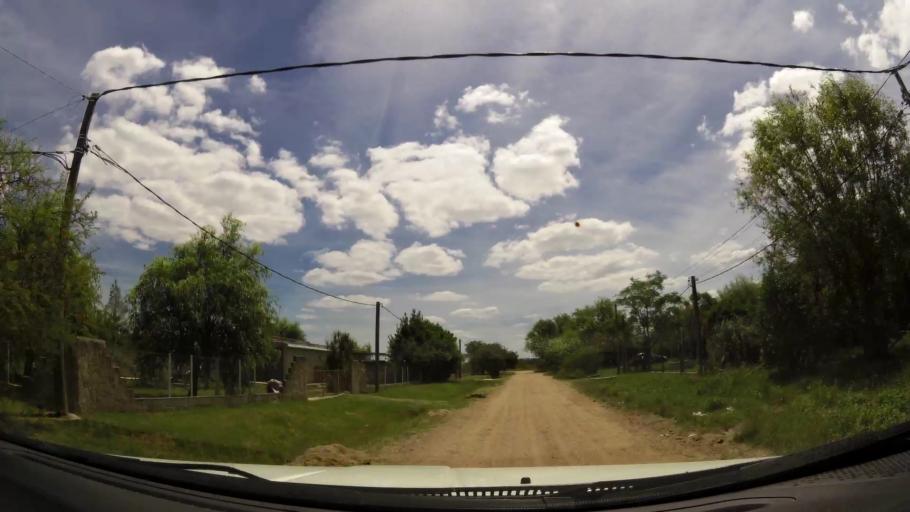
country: UY
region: San Jose
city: Delta del Tigre
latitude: -34.7520
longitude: -56.4237
